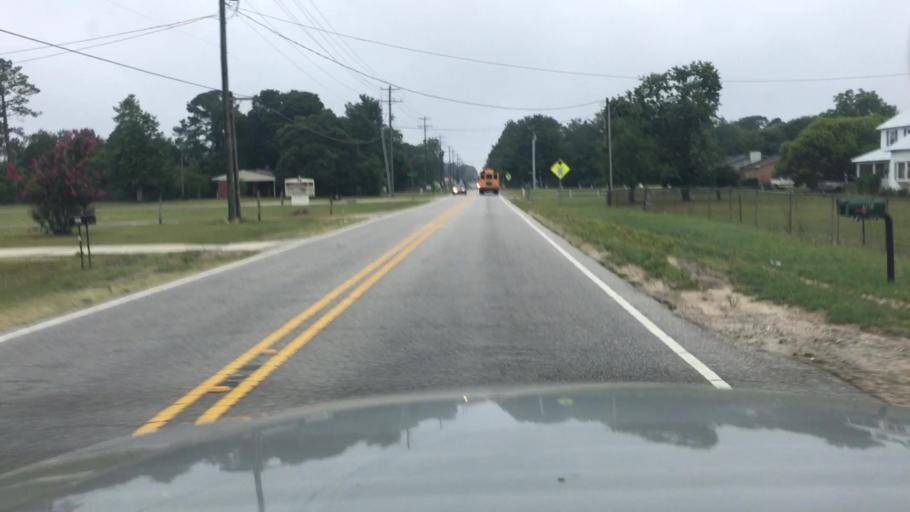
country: US
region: North Carolina
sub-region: Cumberland County
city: Hope Mills
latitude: 34.9762
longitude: -78.9781
